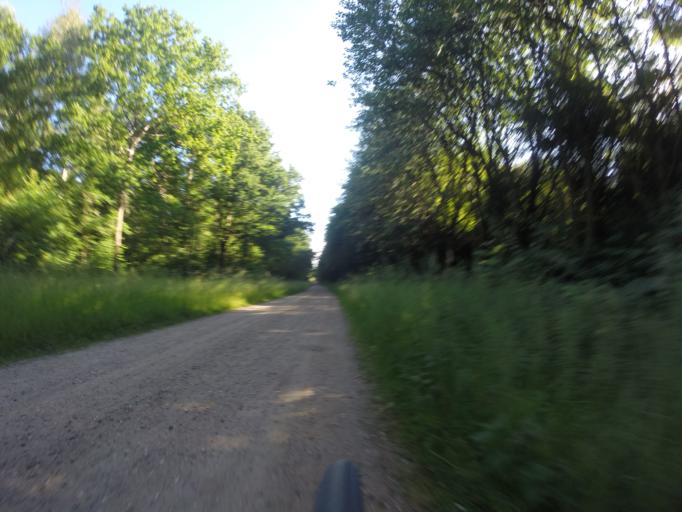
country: DK
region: Capital Region
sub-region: Albertslund Kommune
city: Albertslund
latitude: 55.6911
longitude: 12.3272
